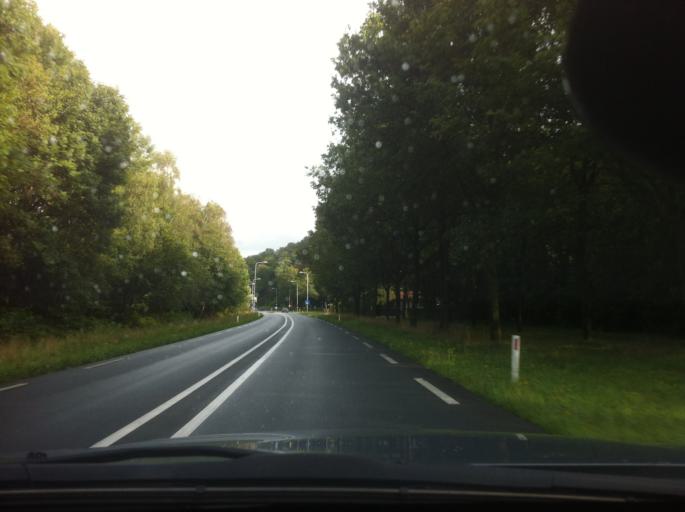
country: NL
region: Gelderland
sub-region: Gemeente Groesbeek
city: Berg en Dal
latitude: 51.8254
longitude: 5.9402
